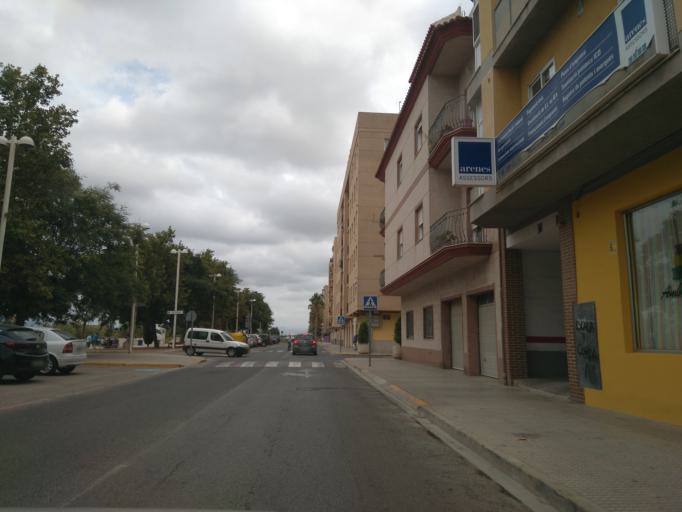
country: ES
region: Valencia
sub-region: Provincia de Valencia
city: Carlet
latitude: 39.2240
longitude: -0.5160
